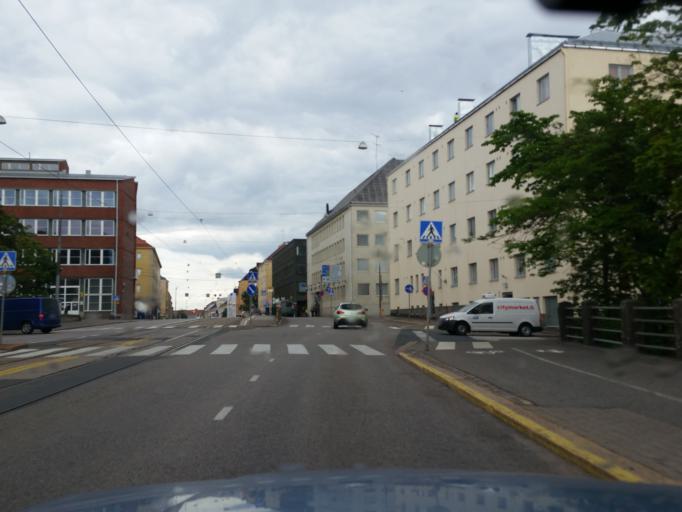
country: FI
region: Uusimaa
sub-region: Helsinki
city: Helsinki
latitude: 60.1929
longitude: 24.9537
